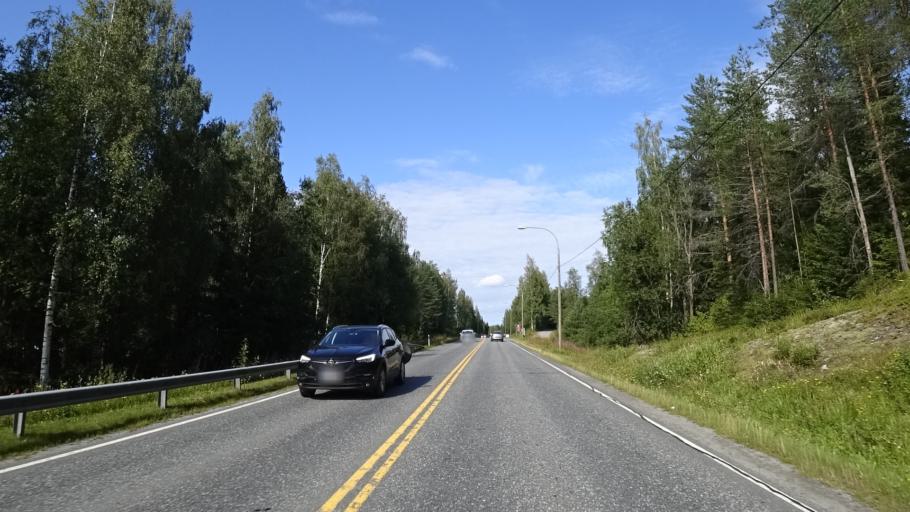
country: FI
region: North Karelia
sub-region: Joensuu
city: Eno
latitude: 62.7866
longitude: 30.0798
